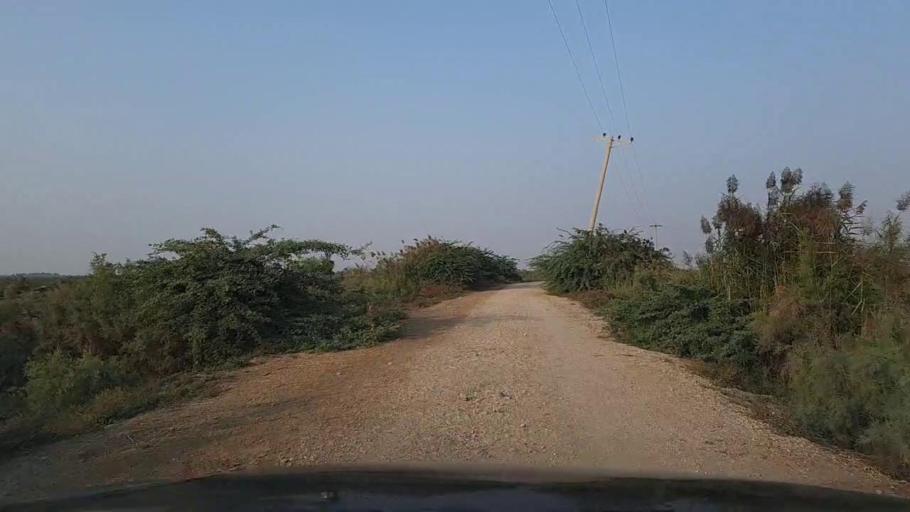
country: PK
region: Sindh
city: Mirpur Sakro
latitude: 24.4160
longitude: 67.7329
